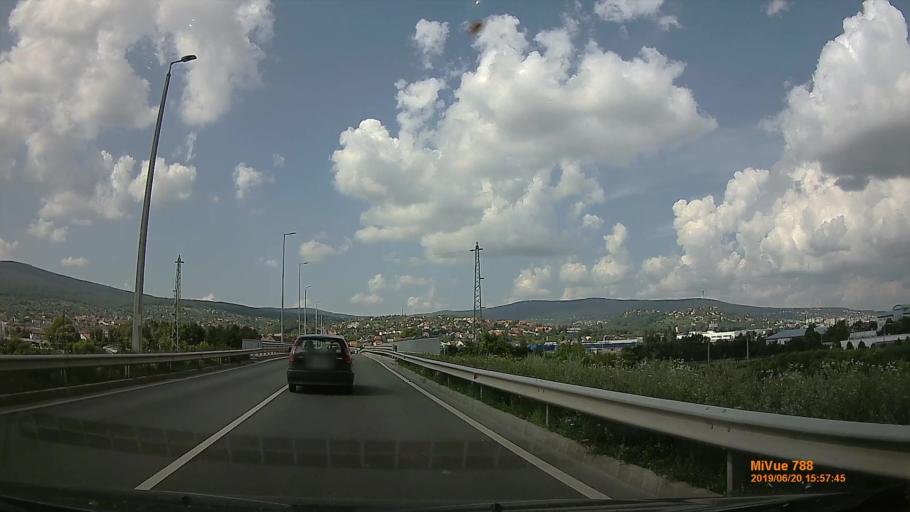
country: HU
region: Baranya
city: Pellerd
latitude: 46.0580
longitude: 18.1754
